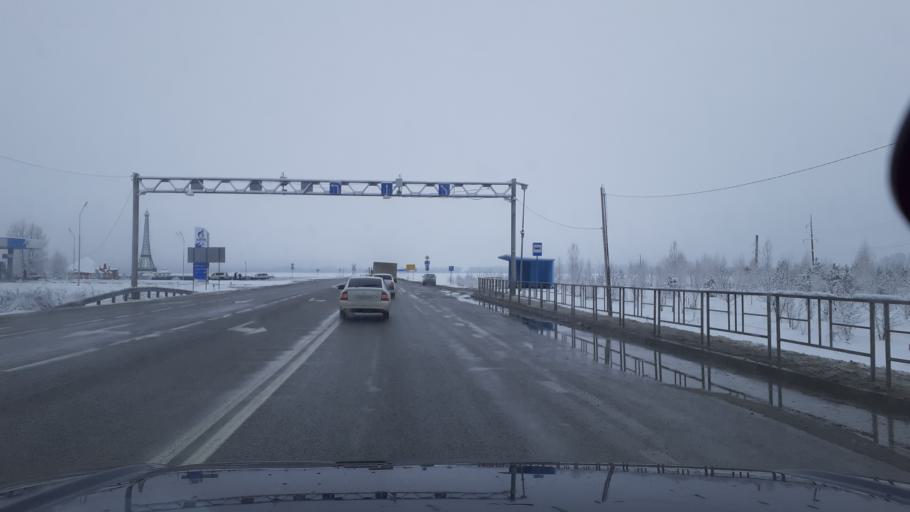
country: RU
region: Adygeya
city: Tul'skiy
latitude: 44.4940
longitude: 40.1646
